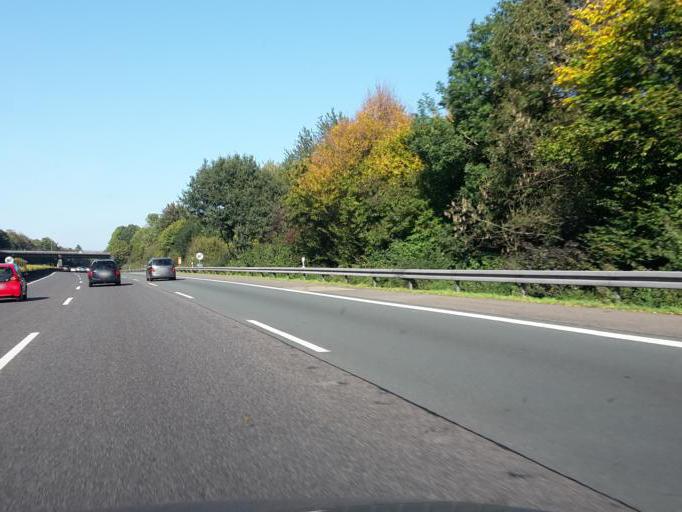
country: DE
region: North Rhine-Westphalia
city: Burscheid
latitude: 51.1008
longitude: 7.1419
